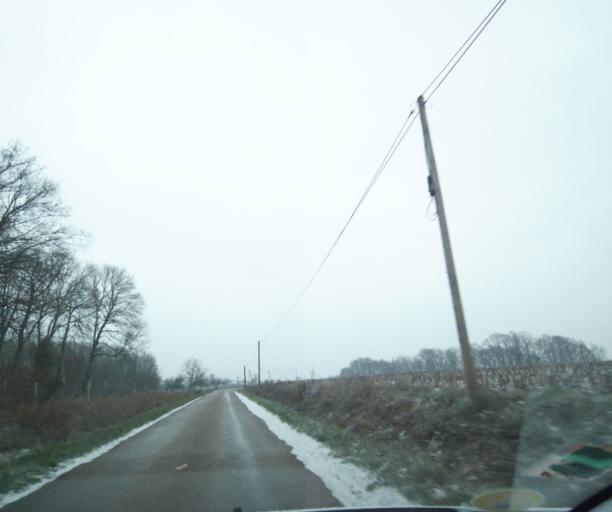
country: FR
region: Champagne-Ardenne
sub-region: Departement de la Haute-Marne
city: Wassy
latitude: 48.4650
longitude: 5.0346
